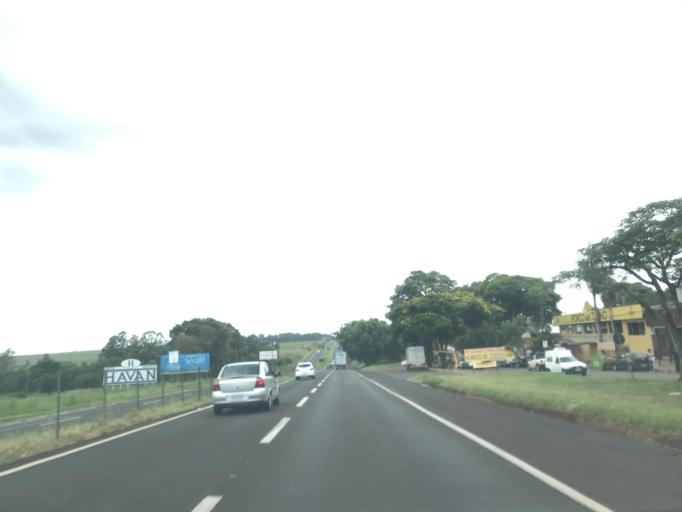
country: BR
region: Parana
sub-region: Mandaguacu
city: Mandaguacu
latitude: -23.3840
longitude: -52.0296
